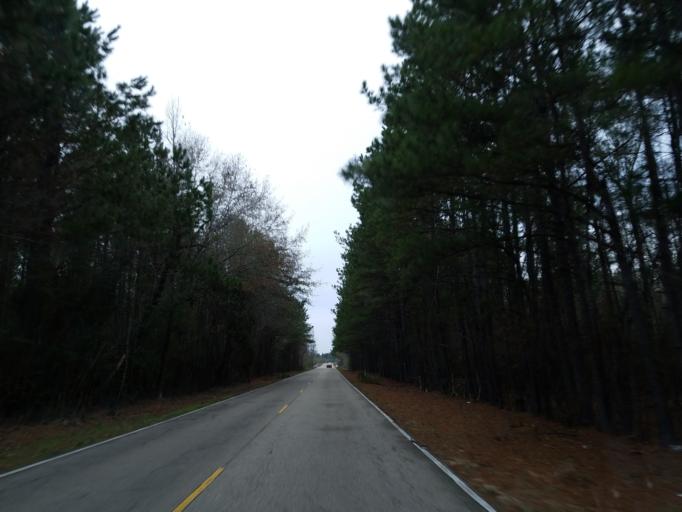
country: US
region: Mississippi
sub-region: Forrest County
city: Hattiesburg
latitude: 31.2676
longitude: -89.2411
